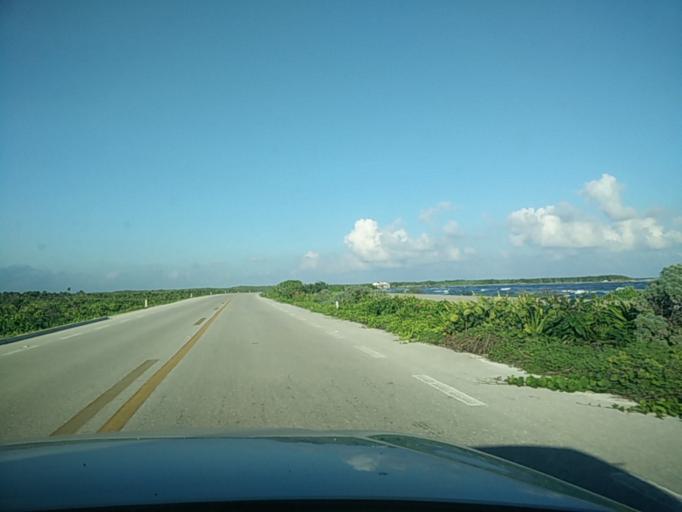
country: MX
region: Quintana Roo
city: San Miguel de Cozumel
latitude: 20.3430
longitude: -86.9095
